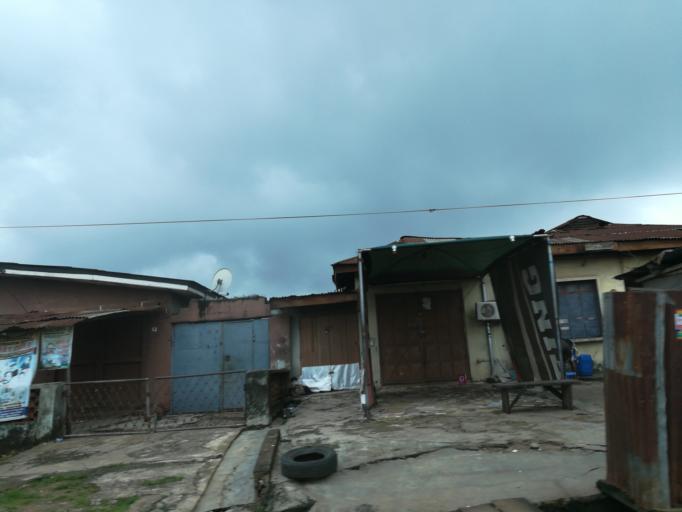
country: NG
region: Lagos
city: Agege
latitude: 6.6106
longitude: 3.3274
